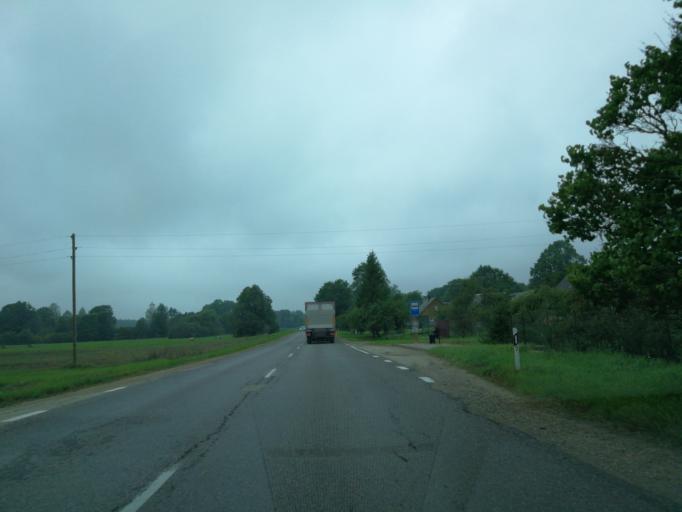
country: LV
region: Livani
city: Livani
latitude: 56.3447
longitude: 26.3290
